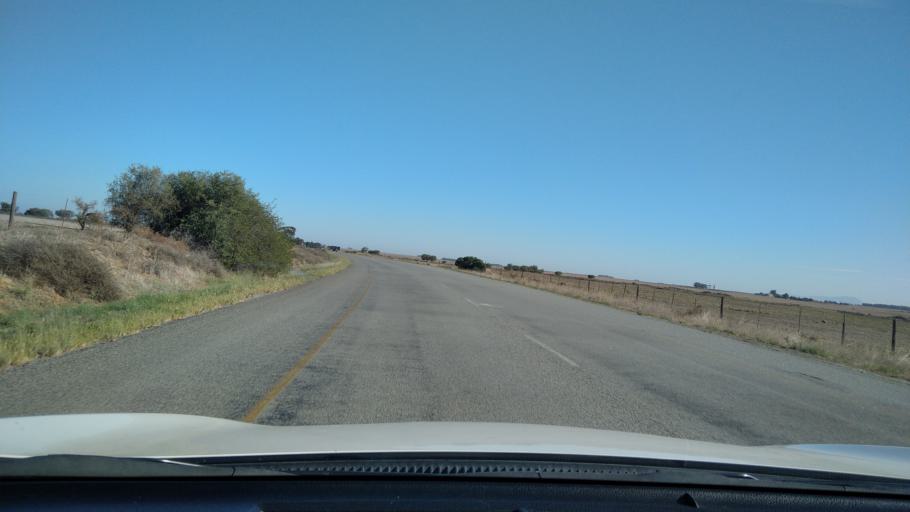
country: ZA
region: Western Cape
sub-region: West Coast District Municipality
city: Moorreesburg
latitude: -33.2594
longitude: 18.5919
